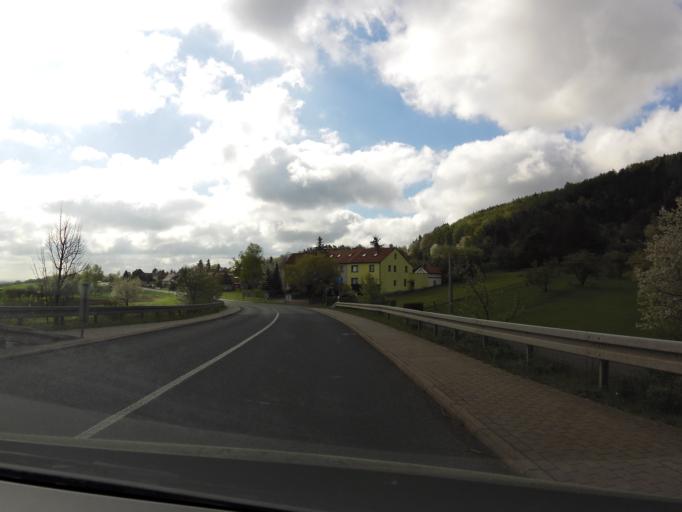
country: DE
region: Thuringia
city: Seebergen
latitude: 50.9299
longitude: 10.7879
